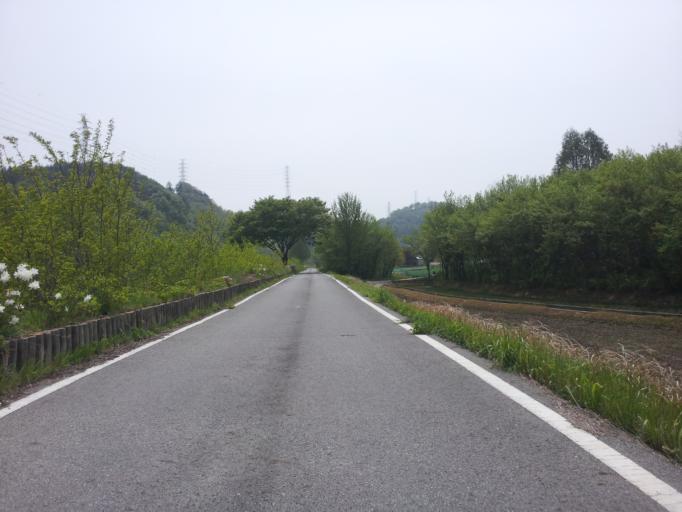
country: KR
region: Daejeon
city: Daejeon
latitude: 36.2617
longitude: 127.2952
